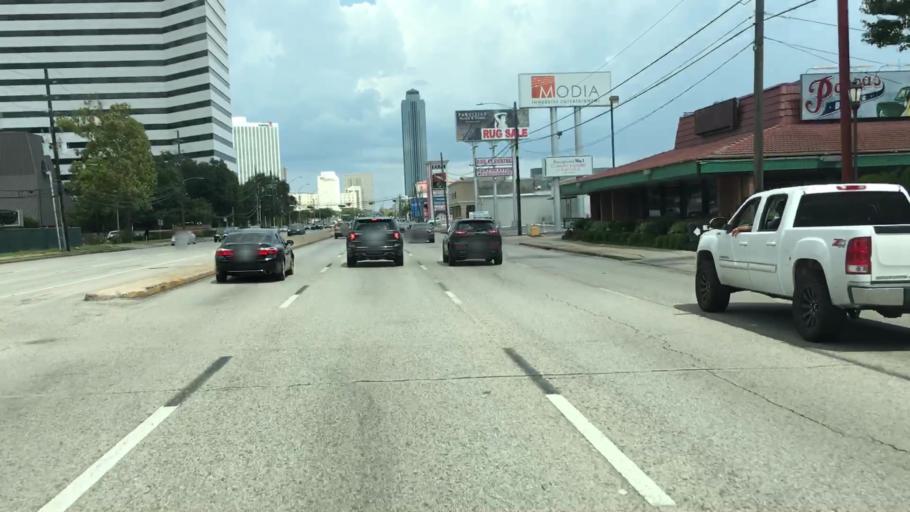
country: US
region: Texas
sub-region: Harris County
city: Hunters Creek Village
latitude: 29.7378
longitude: -95.4815
